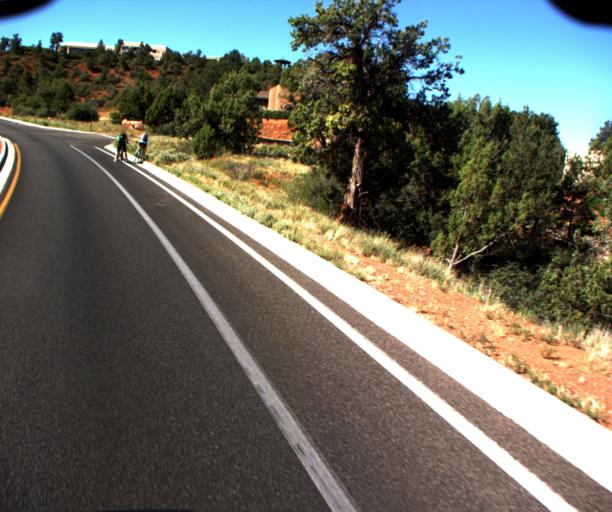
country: US
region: Arizona
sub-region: Coconino County
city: Sedona
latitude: 34.8370
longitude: -111.7773
